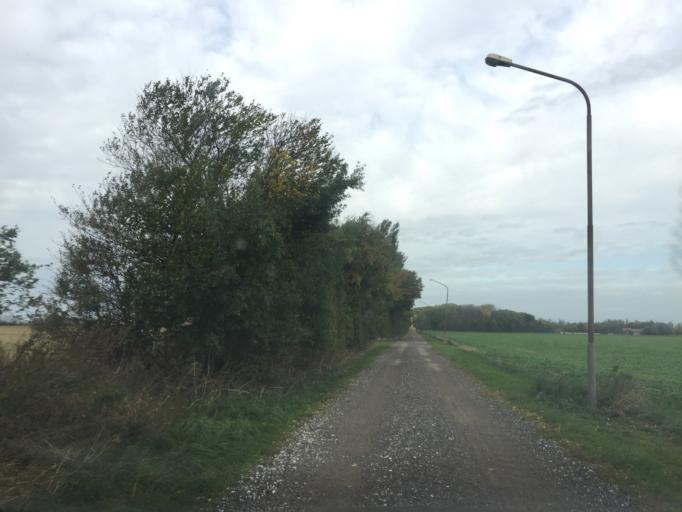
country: DK
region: Zealand
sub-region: Lolland Kommune
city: Rodbyhavn
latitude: 54.6656
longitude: 11.3471
